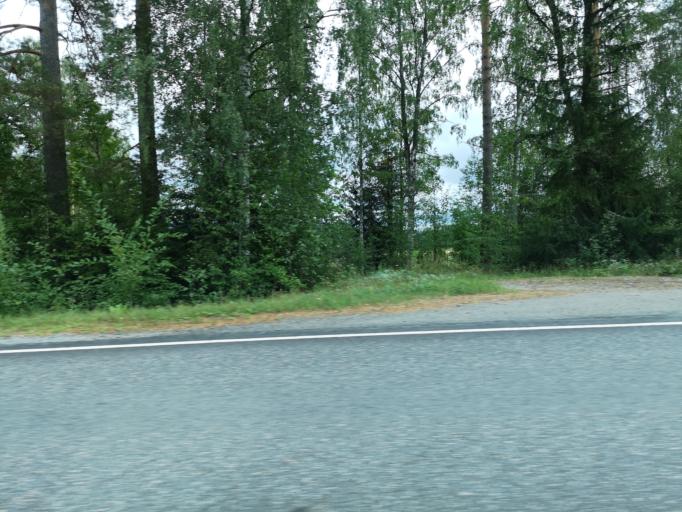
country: FI
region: Central Finland
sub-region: Jyvaeskylae
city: Hankasalmi
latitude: 62.3737
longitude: 26.4424
